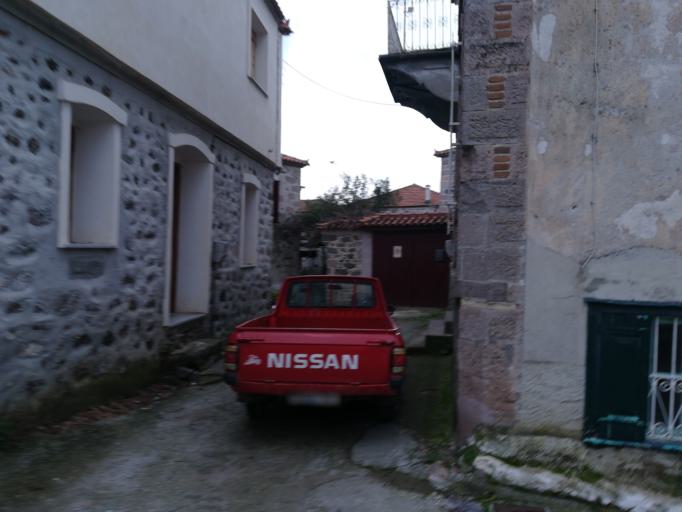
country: GR
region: North Aegean
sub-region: Nomos Lesvou
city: Agia Paraskevi
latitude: 39.2486
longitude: 26.2713
